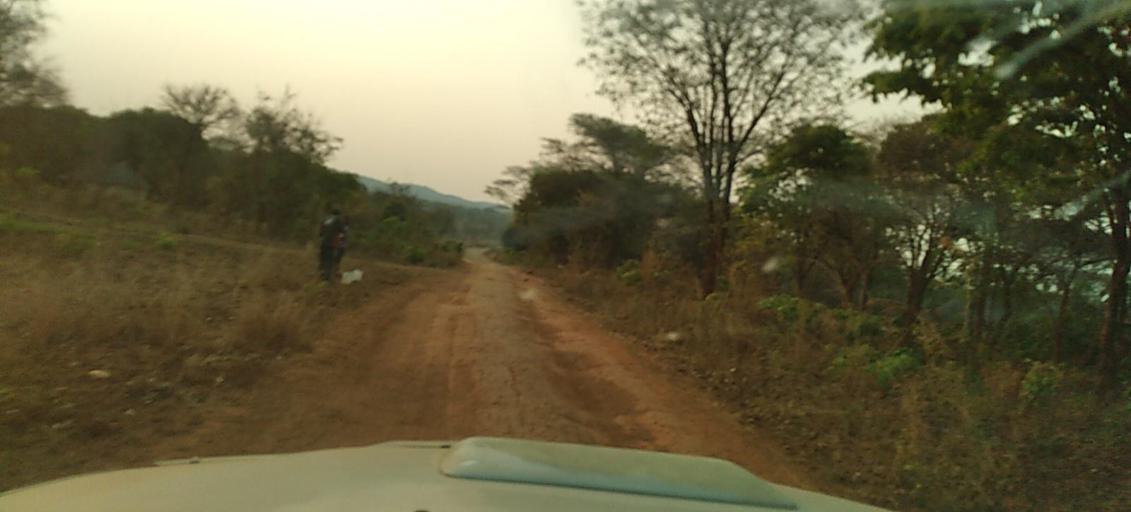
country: ZM
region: North-Western
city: Kasempa
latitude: -13.0725
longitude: 26.3844
